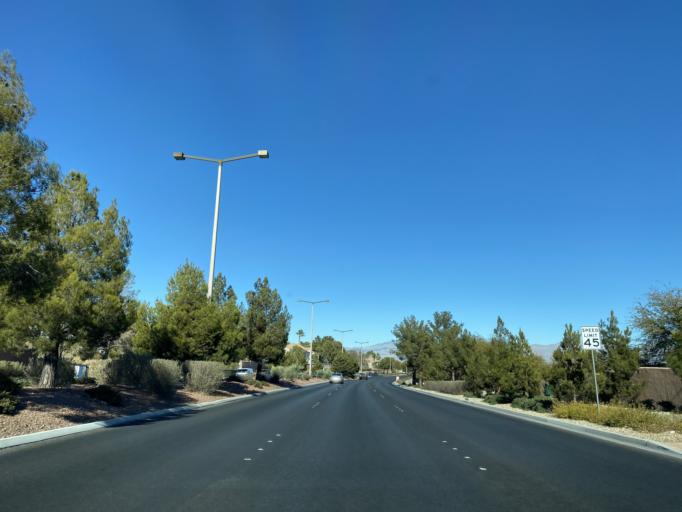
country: US
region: Nevada
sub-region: Clark County
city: Summerlin South
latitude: 36.1897
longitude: -115.2876
